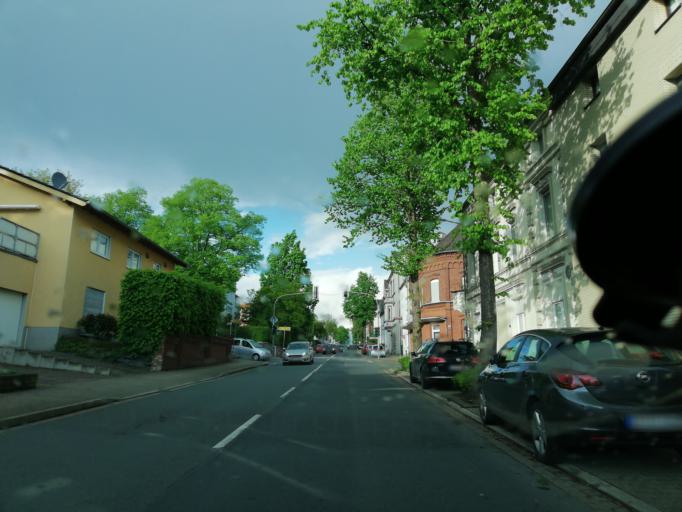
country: DE
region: North Rhine-Westphalia
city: Wetter (Ruhr)
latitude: 51.3856
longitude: 7.3959
